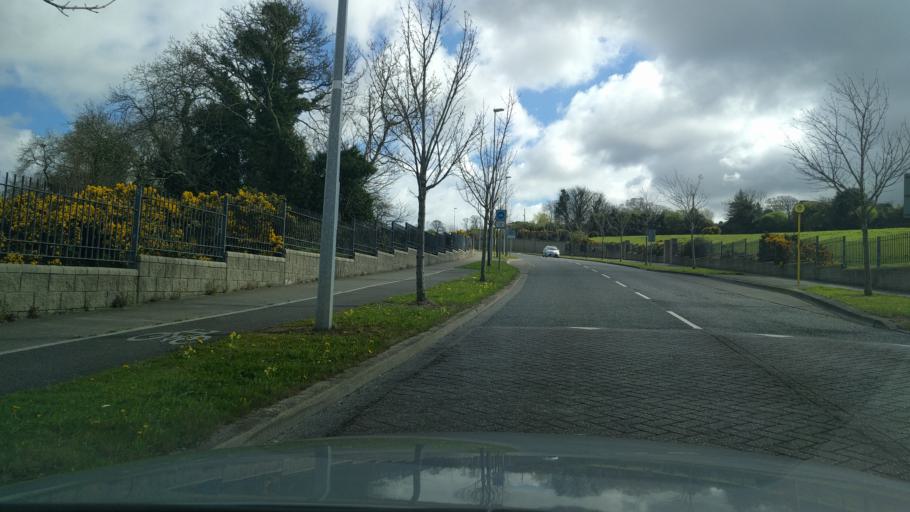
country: IE
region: Leinster
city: Ballyboden
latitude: 53.2731
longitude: -6.3135
